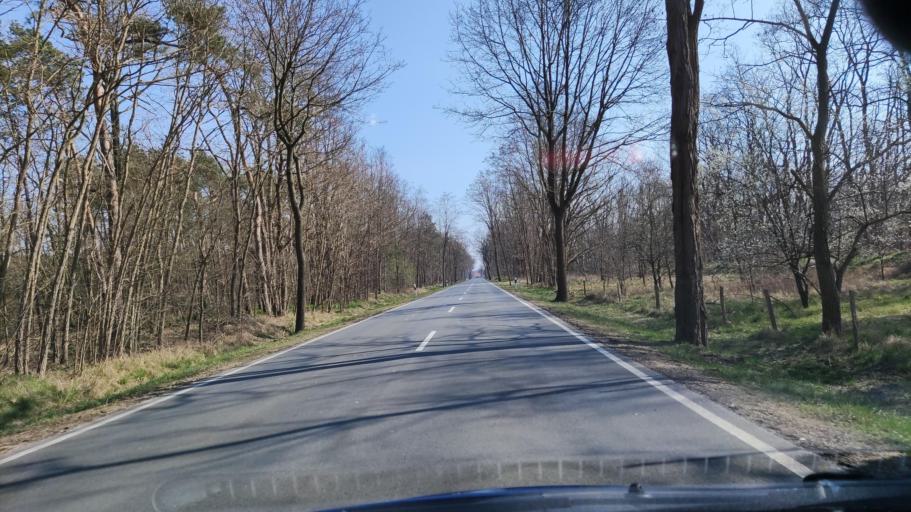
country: DE
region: Lower Saxony
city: Lubbow
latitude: 52.9127
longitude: 11.1670
